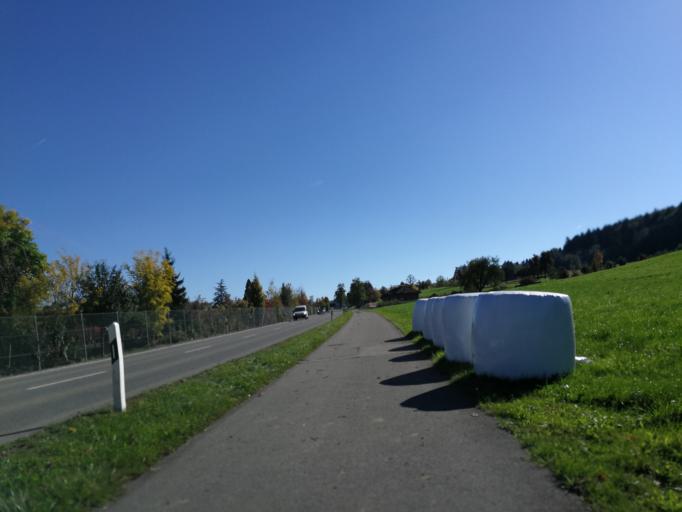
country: CH
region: Zurich
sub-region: Bezirk Uster
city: Egg
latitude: 47.2883
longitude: 8.6945
